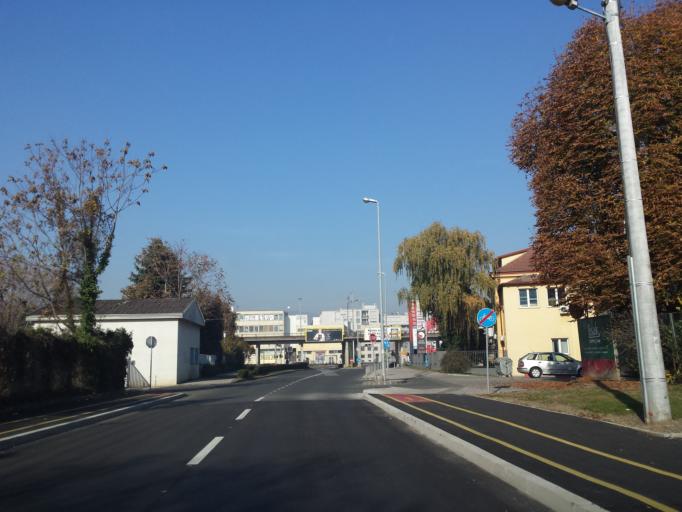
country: HR
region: Grad Zagreb
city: Zagreb
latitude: 45.8068
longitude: 16.0000
